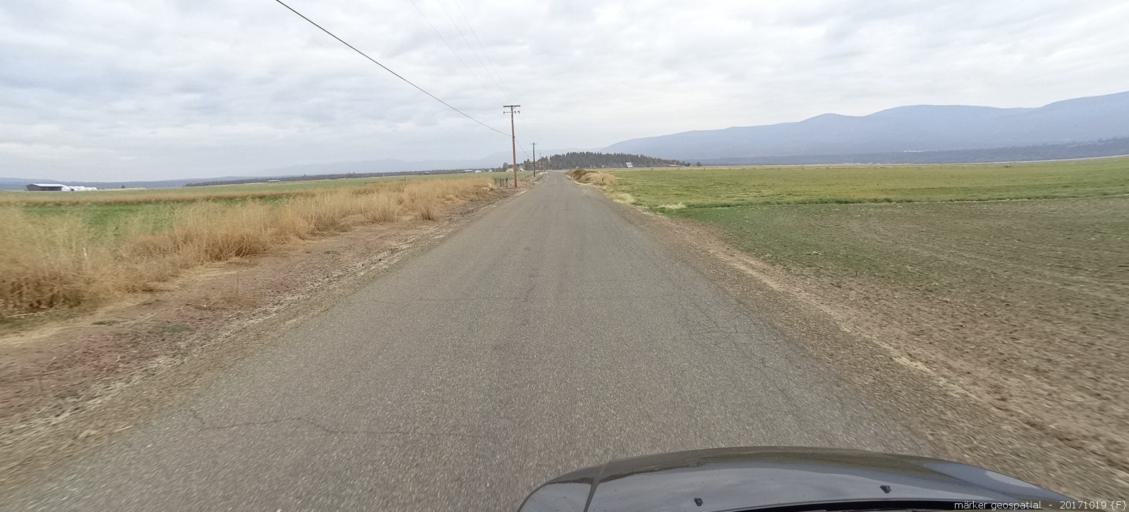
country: US
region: California
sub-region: Shasta County
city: Burney
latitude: 41.0794
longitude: -121.3652
